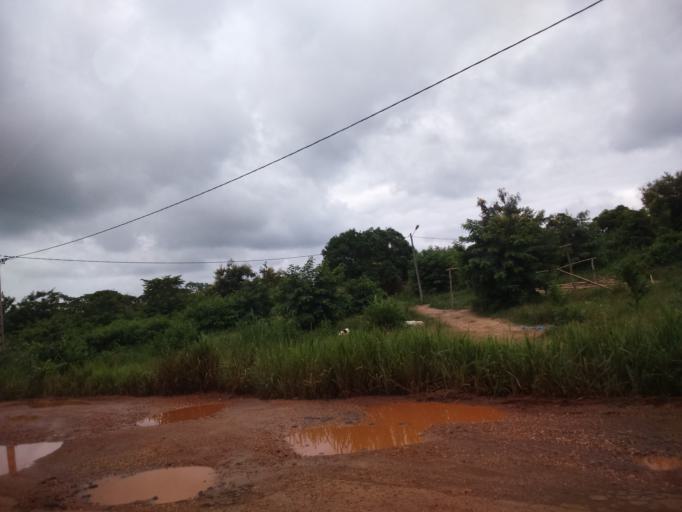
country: CI
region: Moyen-Comoe
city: Abengourou
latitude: 6.6325
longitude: -3.7101
